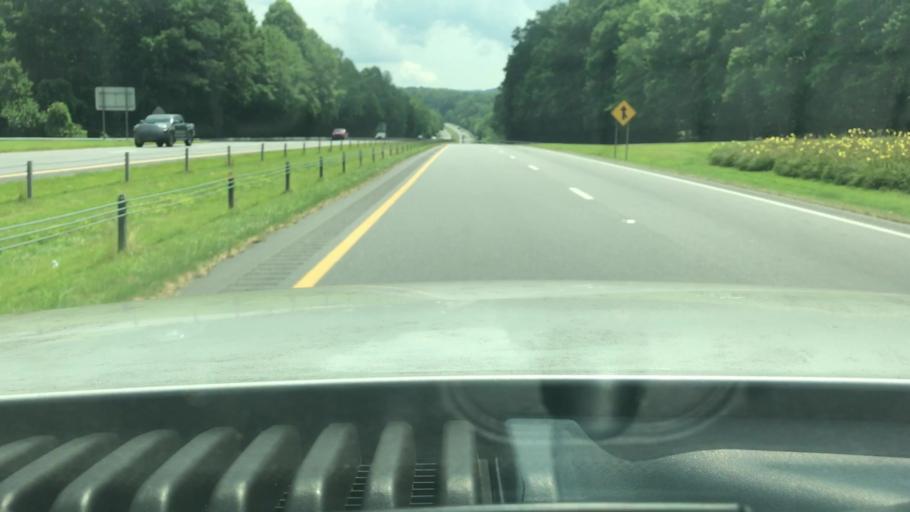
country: US
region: North Carolina
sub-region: Wilkes County
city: Wilkesboro
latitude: 36.1341
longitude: -81.1448
